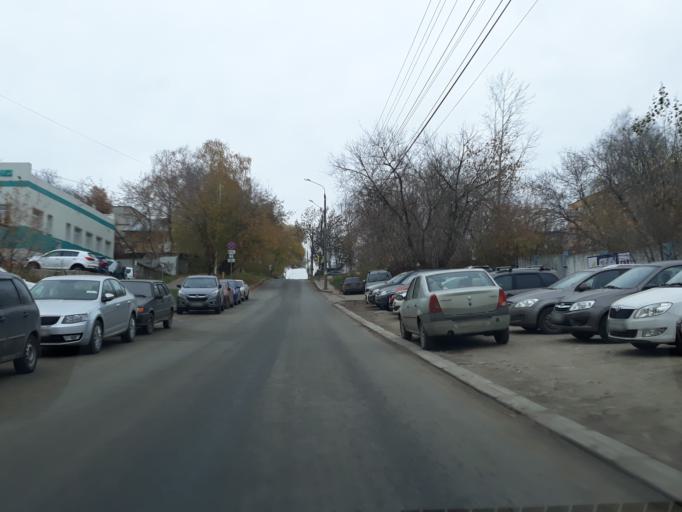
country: RU
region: Nizjnij Novgorod
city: Nizhniy Novgorod
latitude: 56.2493
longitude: 43.9824
